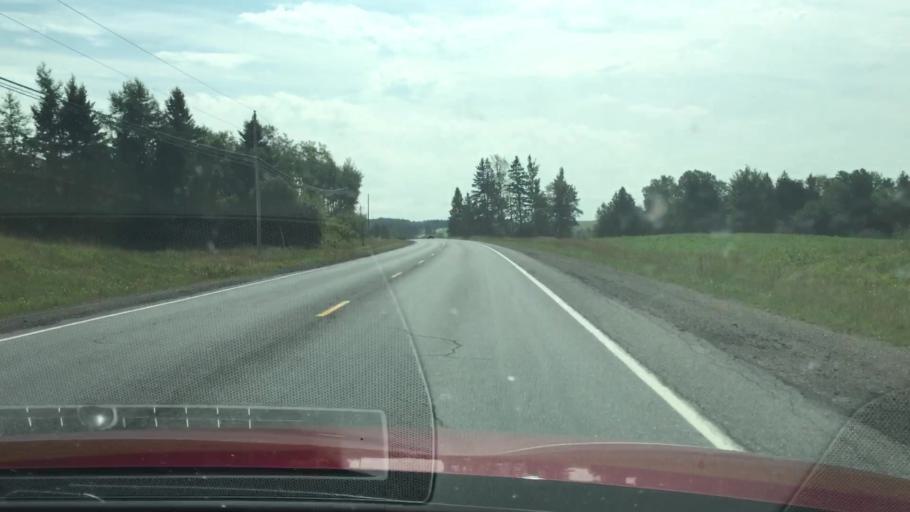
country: US
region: Maine
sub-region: Aroostook County
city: Easton
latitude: 46.6065
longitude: -67.9753
